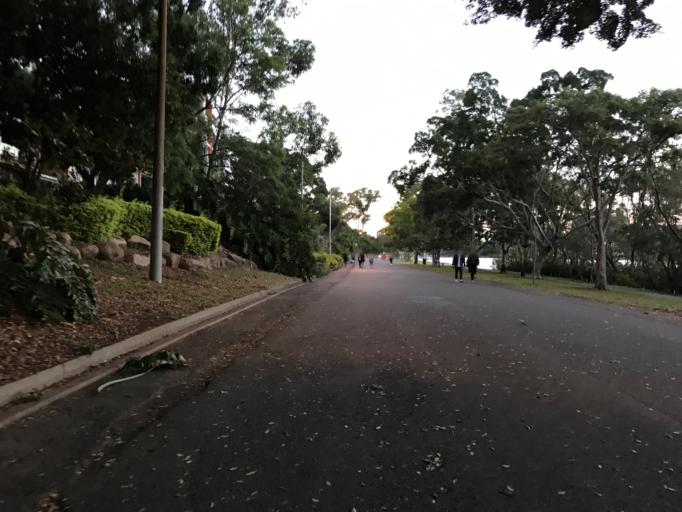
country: AU
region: Queensland
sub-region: Brisbane
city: Milton
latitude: -27.4794
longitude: 153.0024
